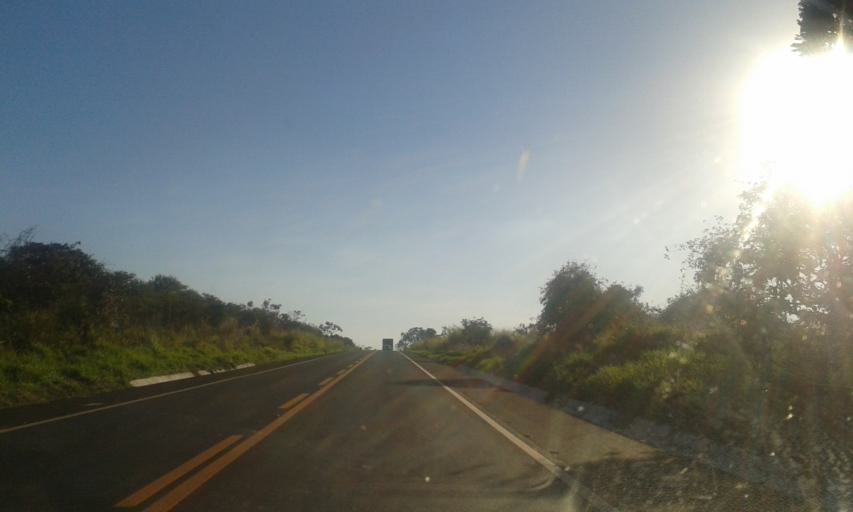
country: BR
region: Minas Gerais
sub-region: Monte Alegre De Minas
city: Monte Alegre de Minas
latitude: -18.8803
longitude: -49.1675
